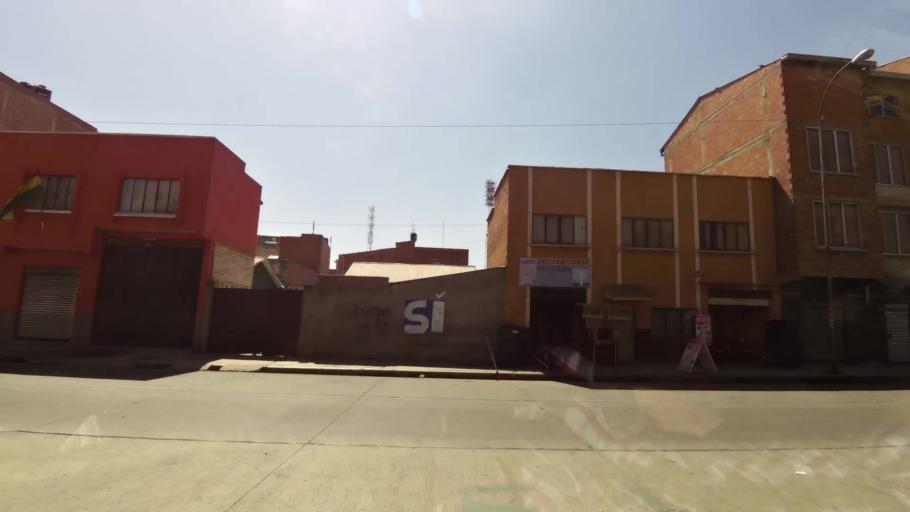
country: BO
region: La Paz
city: La Paz
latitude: -16.5249
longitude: -68.1488
